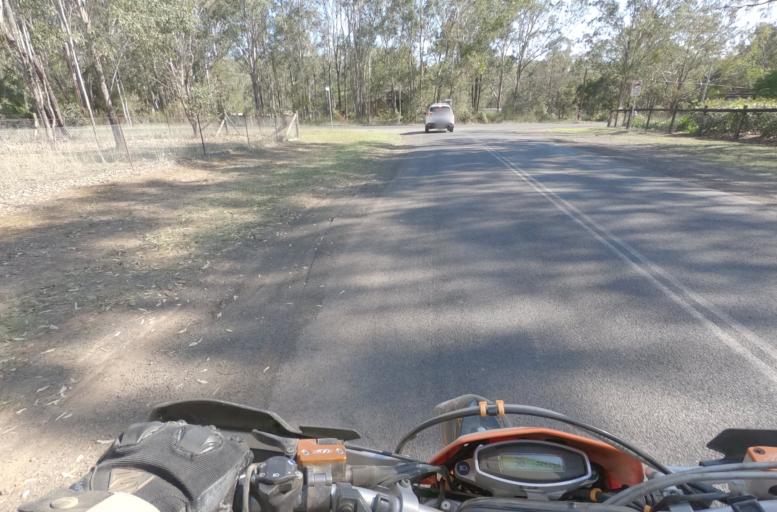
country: AU
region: New South Wales
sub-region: Hawkesbury
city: Pitt Town
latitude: -33.5876
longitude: 150.8708
